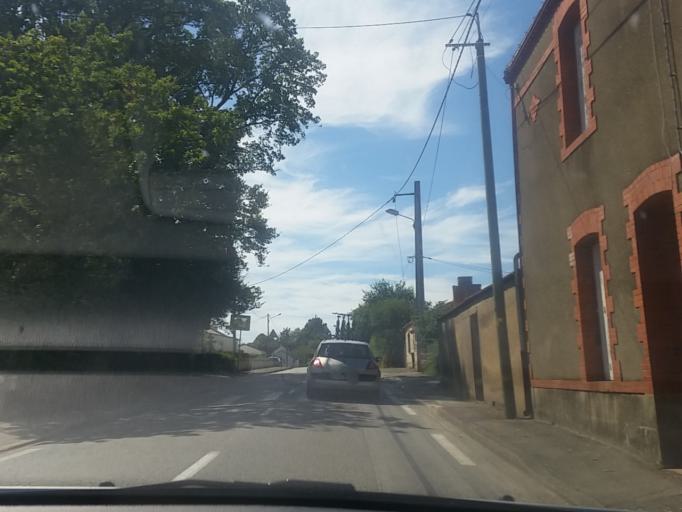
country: FR
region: Pays de la Loire
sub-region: Departement de la Loire-Atlantique
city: Chauve
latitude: 47.1877
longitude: -1.9496
